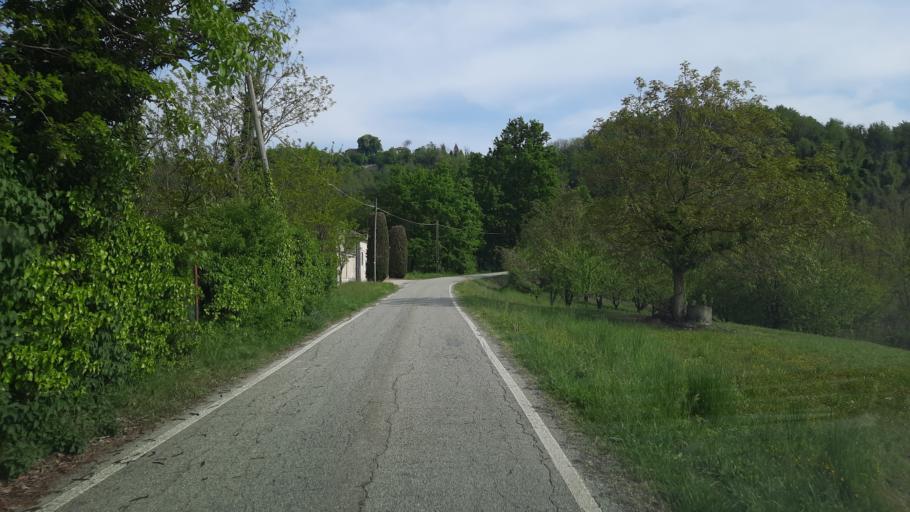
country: IT
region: Piedmont
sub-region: Provincia di Vercelli
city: Palazzolo Vercellese
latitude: 45.1661
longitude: 8.2571
